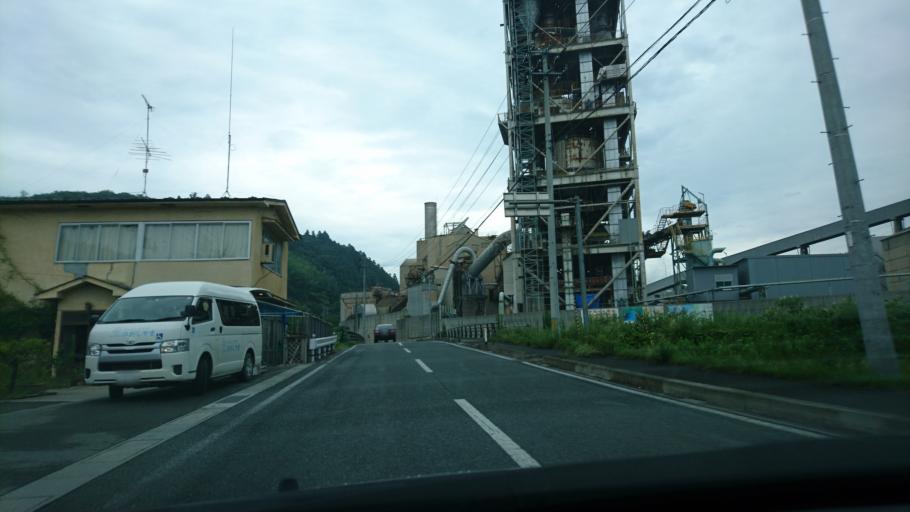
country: JP
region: Iwate
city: Ichinoseki
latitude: 38.9828
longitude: 141.2433
